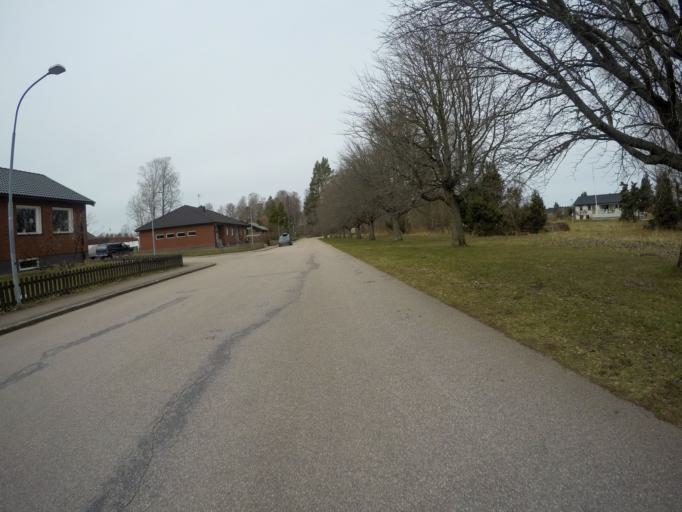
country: SE
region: Vaestmanland
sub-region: Vasteras
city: Vasteras
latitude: 59.5953
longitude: 16.6090
